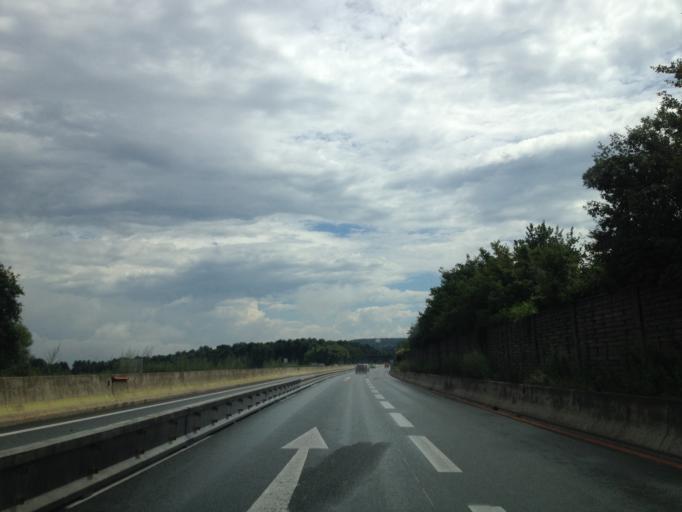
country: AT
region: Styria
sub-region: Politischer Bezirk Hartberg-Fuerstenfeld
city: Bad Waltersdorf
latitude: 47.1851
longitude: 15.9977
